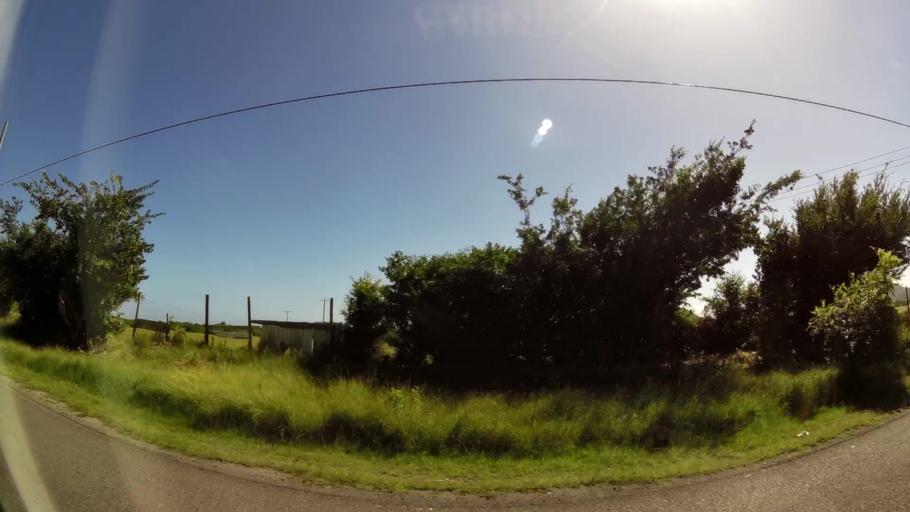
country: LC
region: Vieux-Fort
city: Vieux Fort
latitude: 13.7480
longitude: -60.9509
